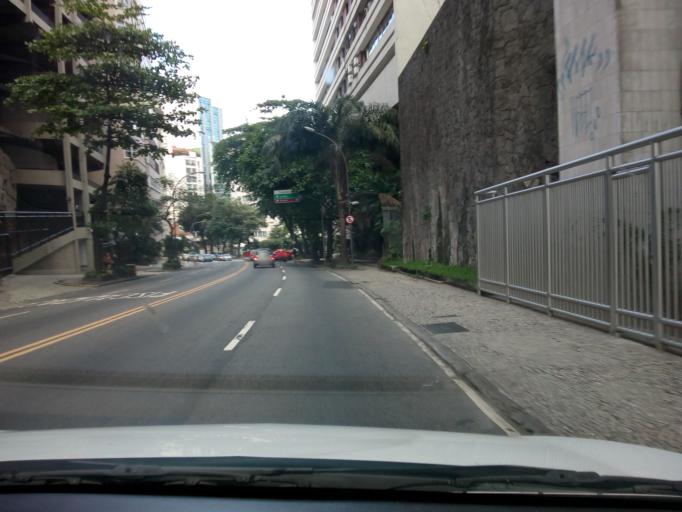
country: BR
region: Rio de Janeiro
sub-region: Rio De Janeiro
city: Rio de Janeiro
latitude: -22.9772
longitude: -43.1955
